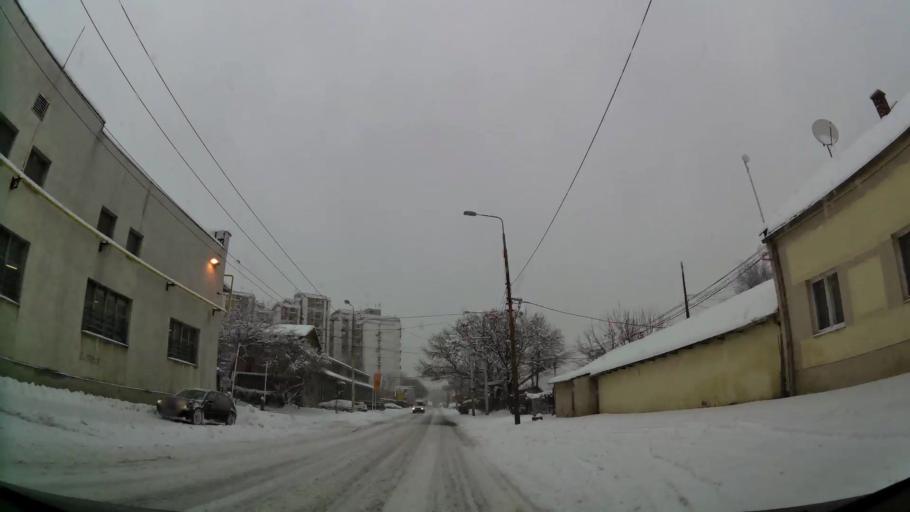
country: RS
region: Central Serbia
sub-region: Belgrade
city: Stari Grad
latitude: 44.8254
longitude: 20.4662
